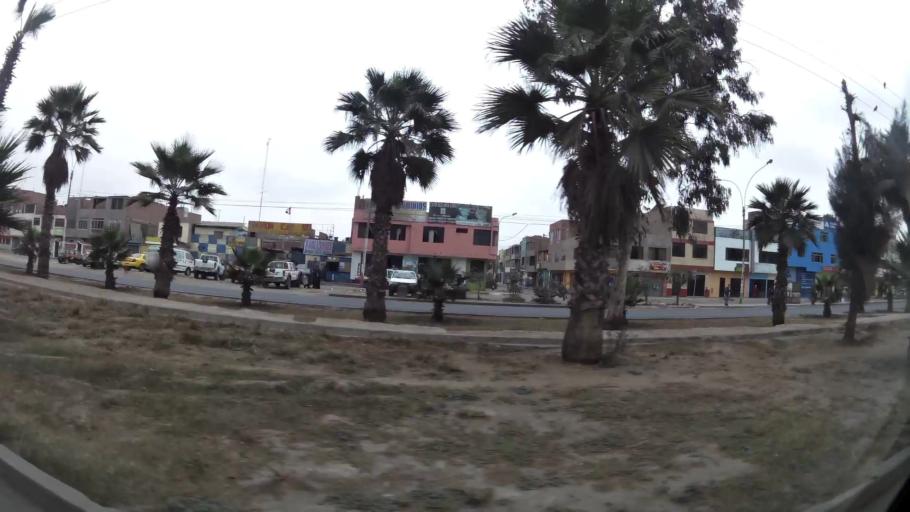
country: PE
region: Lima
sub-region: Lima
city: Independencia
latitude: -11.9501
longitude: -77.0601
